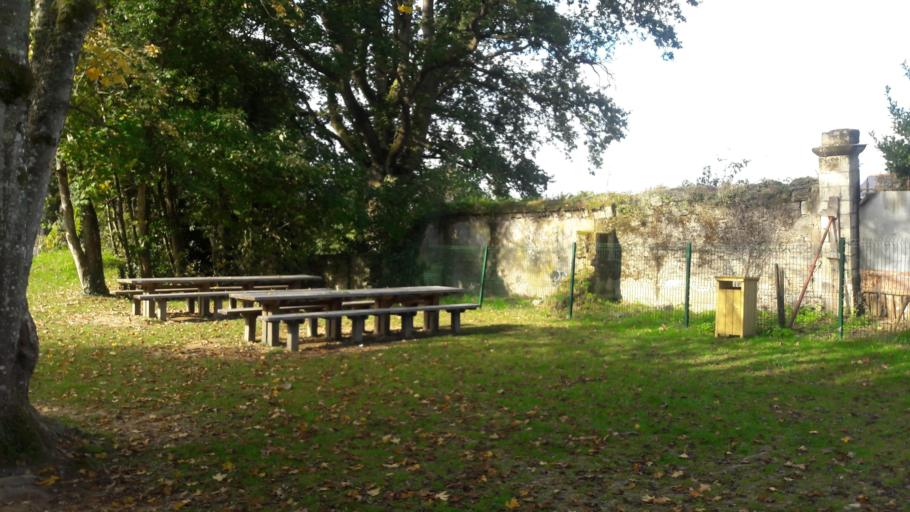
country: FR
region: Pays de la Loire
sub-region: Departement de la Loire-Atlantique
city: Treillieres
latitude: 47.3233
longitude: -1.6221
